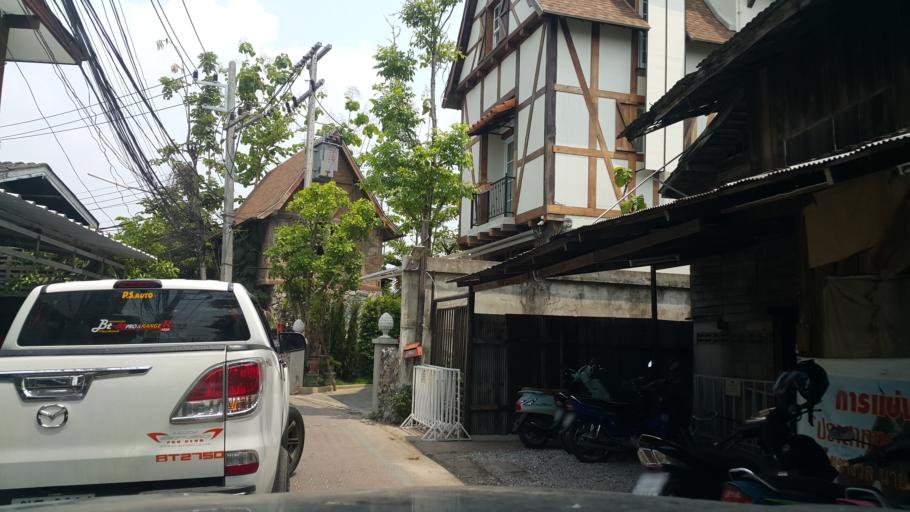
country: TH
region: Chiang Mai
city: Chiang Mai
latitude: 18.7907
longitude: 98.9814
